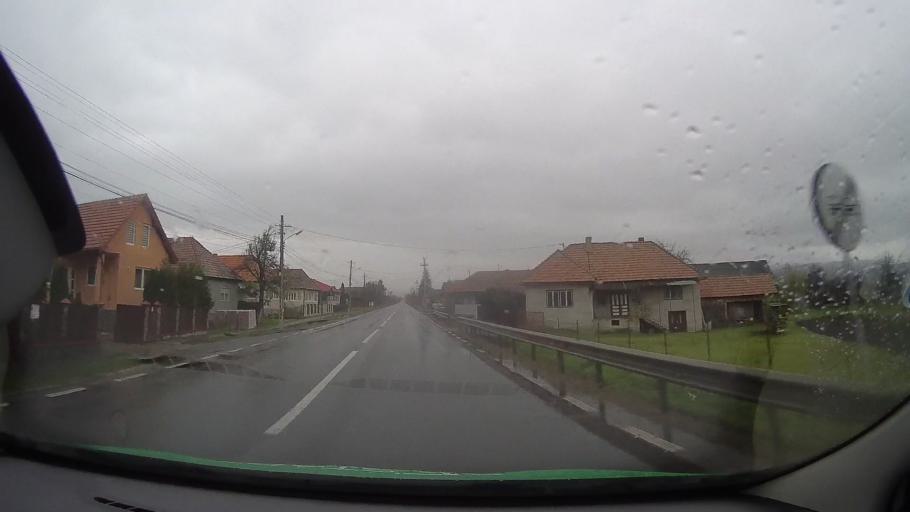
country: RO
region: Mures
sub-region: Comuna Alunis
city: Alunis
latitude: 46.8953
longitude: 24.8033
